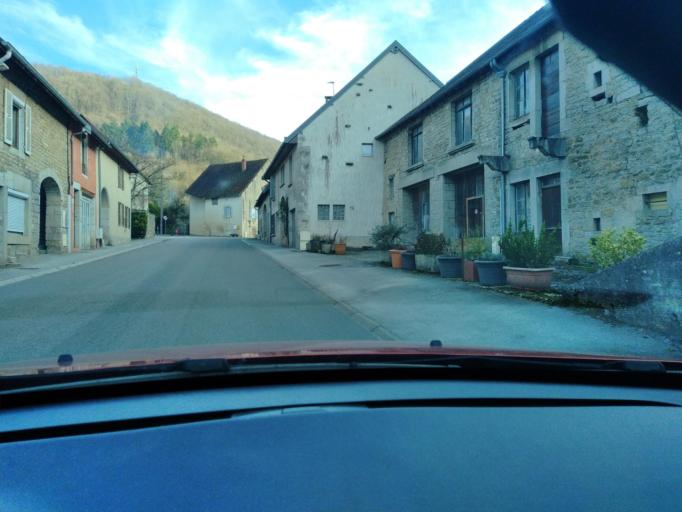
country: FR
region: Franche-Comte
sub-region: Departement du Jura
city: Perrigny
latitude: 46.6338
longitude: 5.6076
